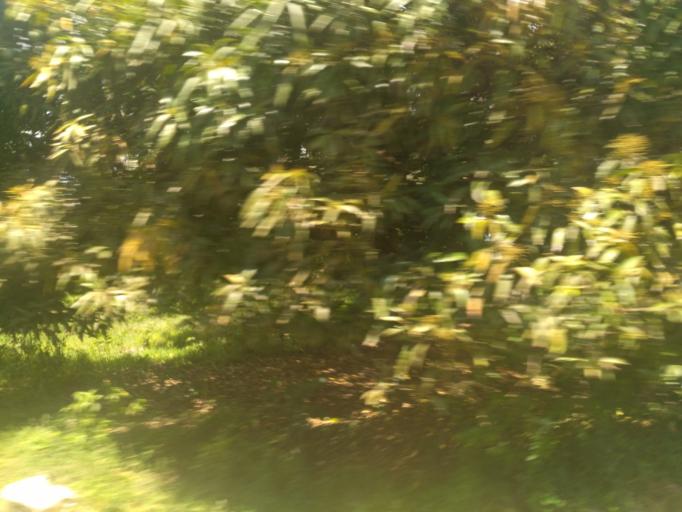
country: TZ
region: Zanzibar North
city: Gamba
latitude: -5.9298
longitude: 39.3418
